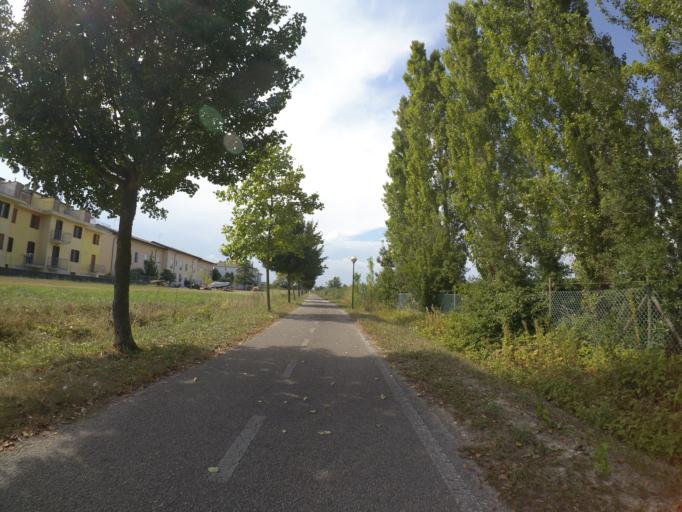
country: IT
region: Friuli Venezia Giulia
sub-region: Provincia di Udine
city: Lignano Sabbiadoro
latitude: 45.6643
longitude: 13.0739
